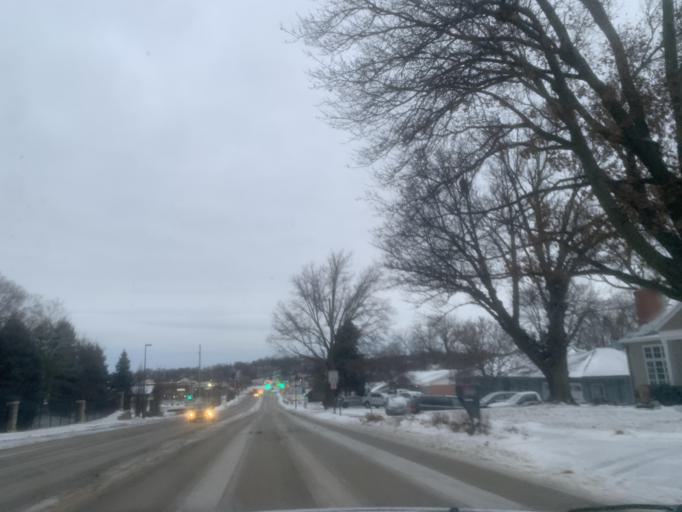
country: US
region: Nebraska
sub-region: Douglas County
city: Ralston
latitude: 41.2379
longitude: -96.0527
